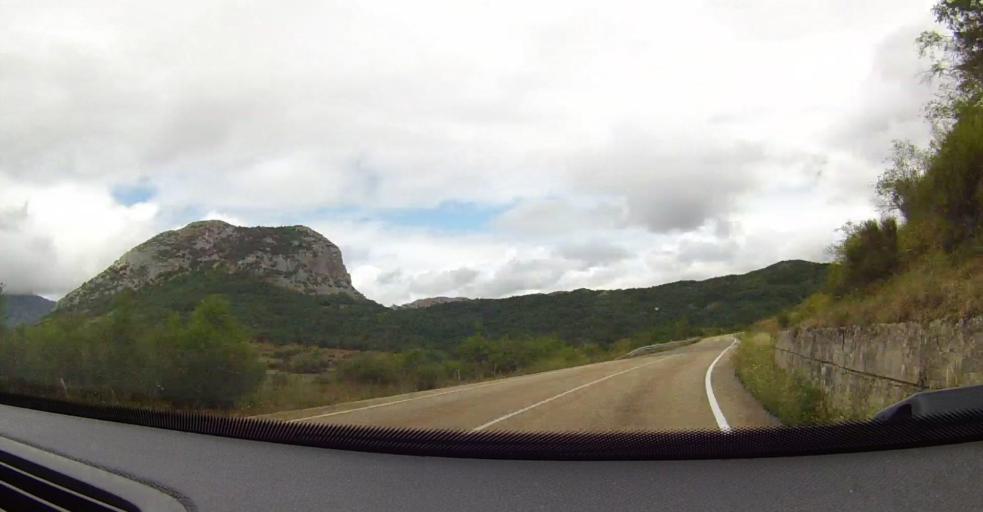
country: ES
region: Castille and Leon
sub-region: Provincia de Leon
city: Reyero
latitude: 42.9425
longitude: -5.2597
